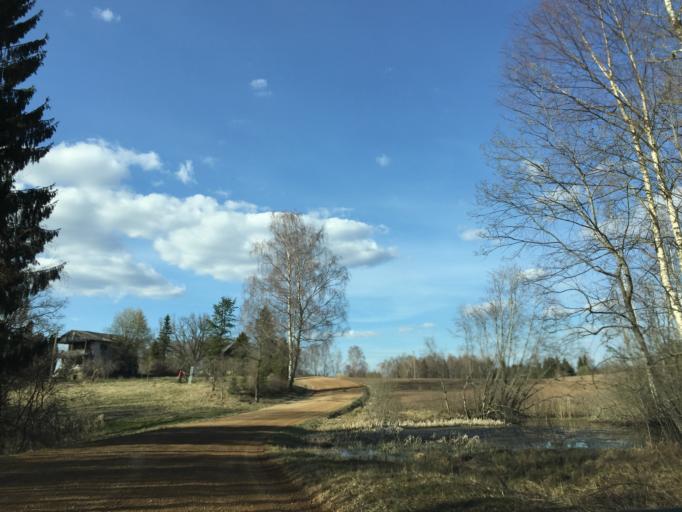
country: EE
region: Tartu
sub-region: Elva linn
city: Elva
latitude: 58.0931
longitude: 26.5112
